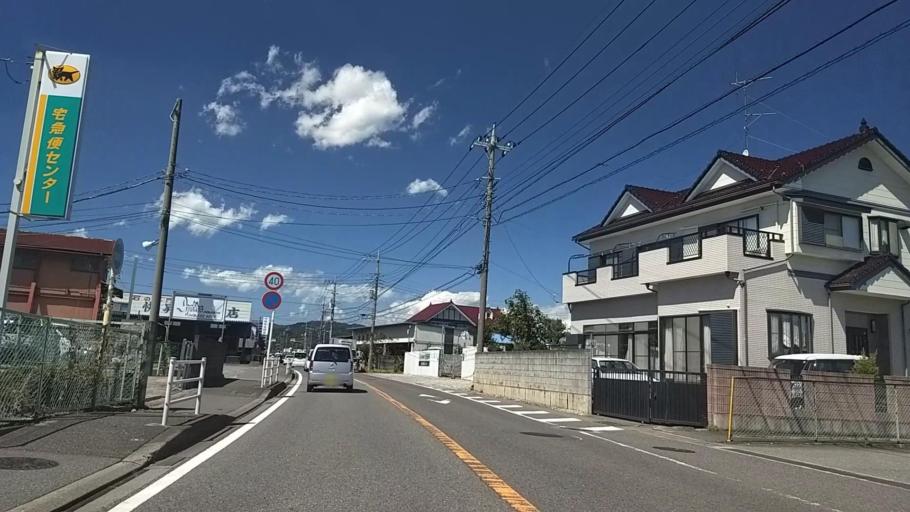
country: JP
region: Tokyo
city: Hachioji
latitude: 35.5815
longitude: 139.3138
